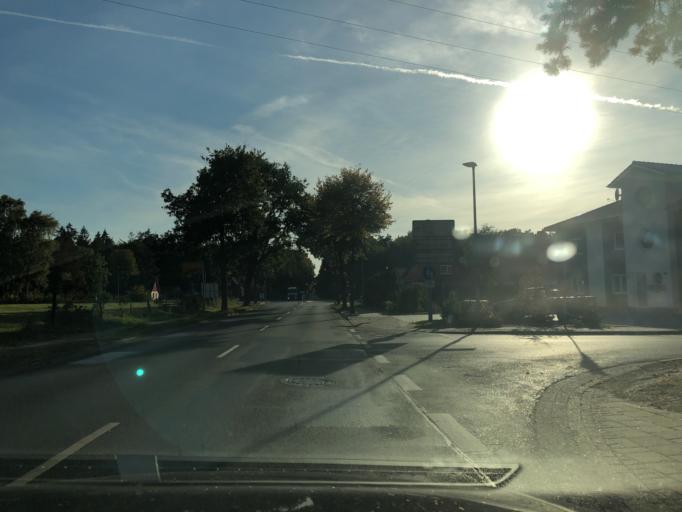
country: DE
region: Lower Saxony
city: Papenburg
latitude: 53.0641
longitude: 7.4141
